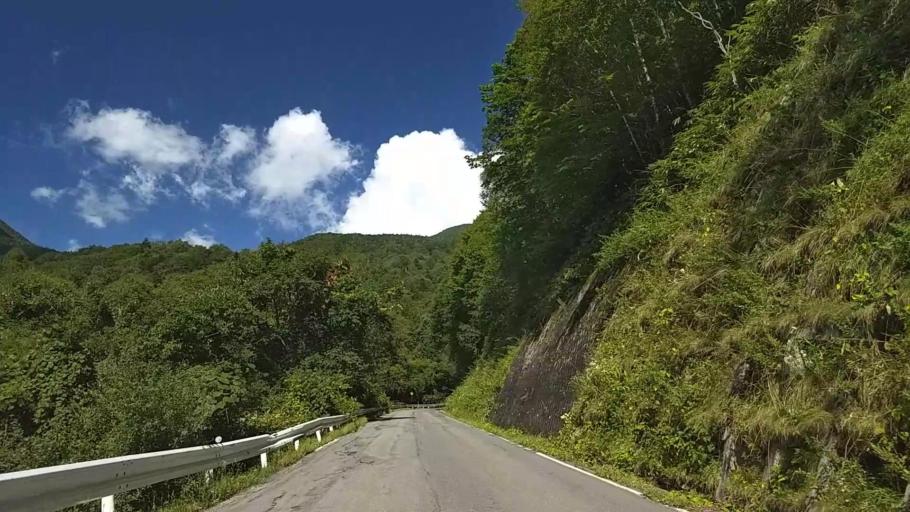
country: JP
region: Nagano
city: Chino
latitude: 36.0784
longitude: 138.2919
